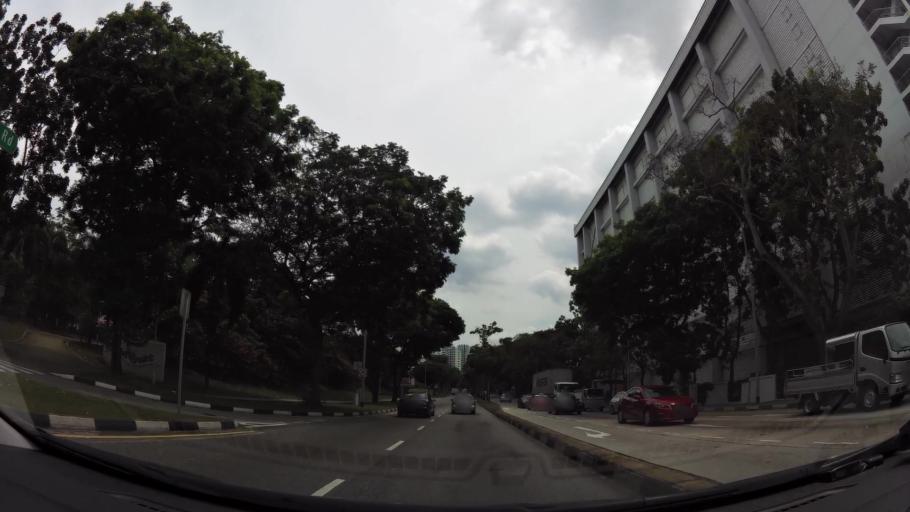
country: MY
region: Johor
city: Johor Bahru
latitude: 1.3373
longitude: 103.7176
